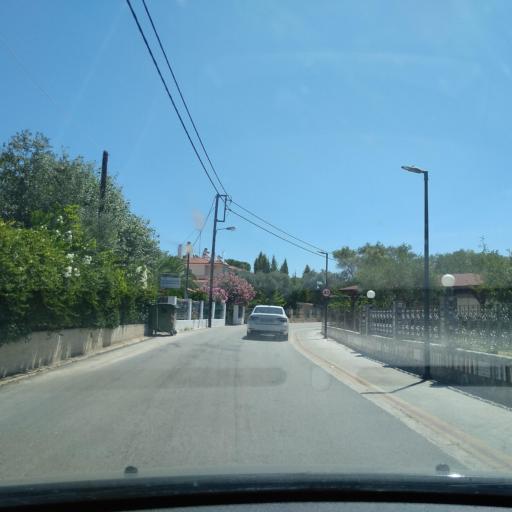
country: GR
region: Central Macedonia
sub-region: Nomos Chalkidikis
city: Neos Marmaras
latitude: 40.1880
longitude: 23.7837
